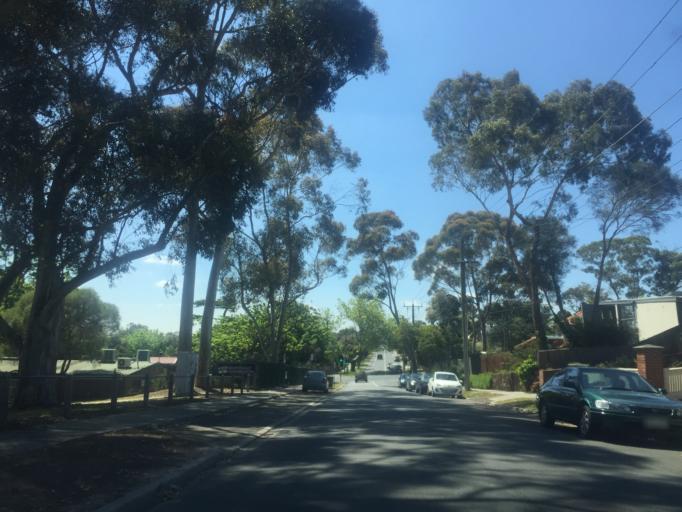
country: AU
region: Victoria
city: Mont Albert
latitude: -37.8049
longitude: 145.0969
